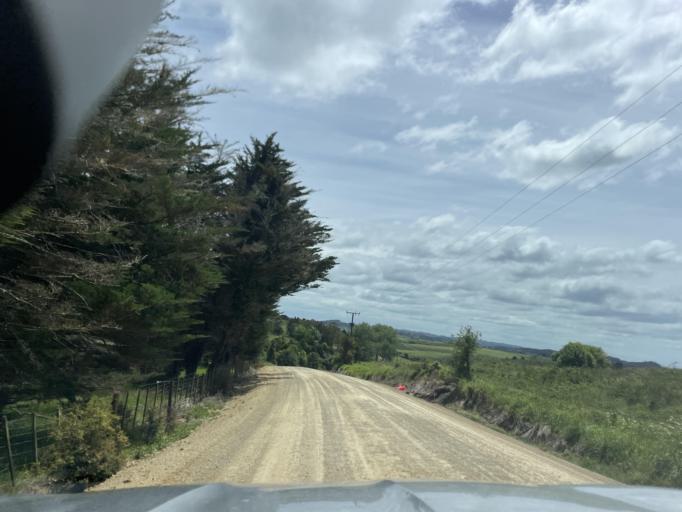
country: NZ
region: Auckland
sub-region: Auckland
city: Wellsford
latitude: -36.1480
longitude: 174.2818
